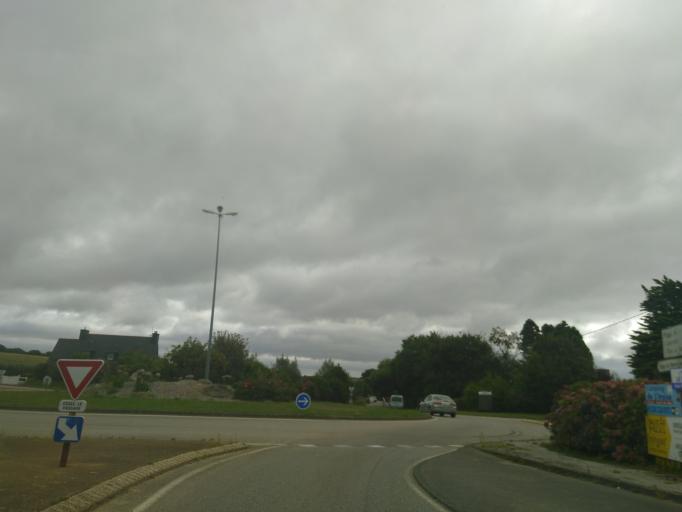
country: FR
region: Brittany
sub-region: Departement du Finistere
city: Plomodiern
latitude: 48.1673
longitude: -4.2679
